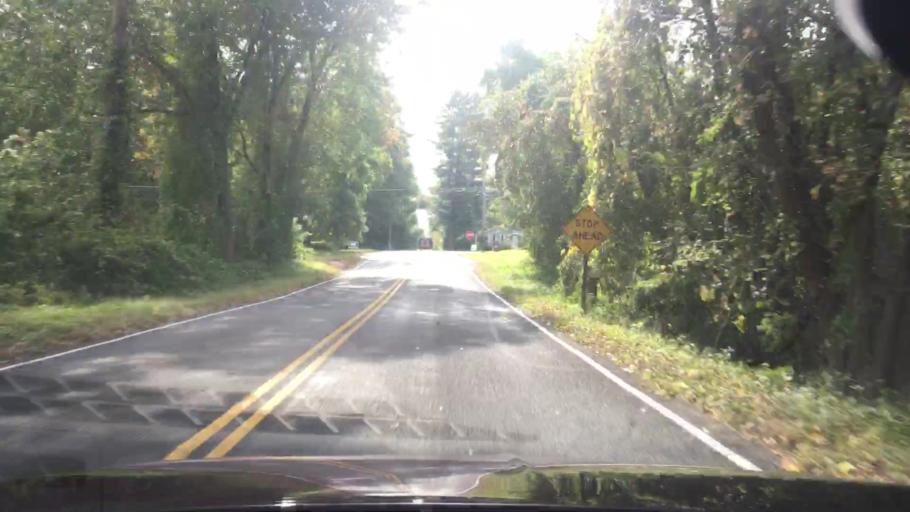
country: US
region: Connecticut
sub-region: Tolland County
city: Somers
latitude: 41.9537
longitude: -72.4826
